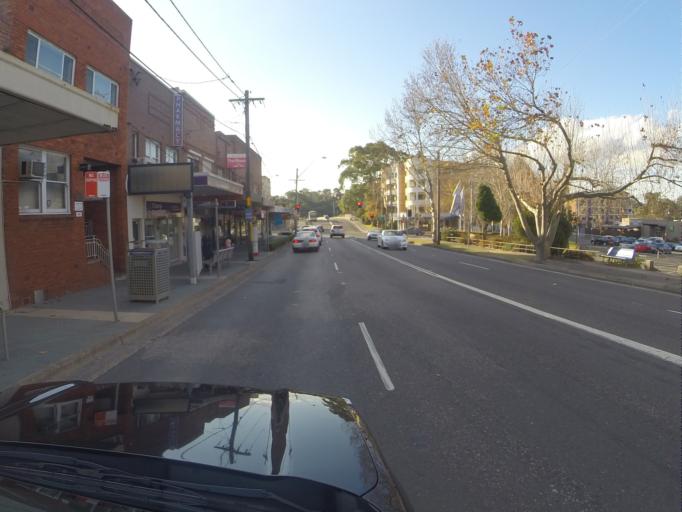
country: AU
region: New South Wales
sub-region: Rockdale
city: Bexley North
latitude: -33.9389
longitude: 151.1142
